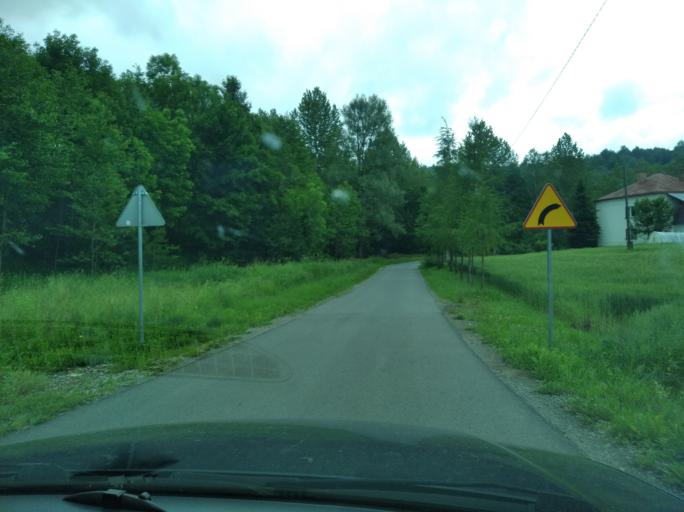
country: PL
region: Subcarpathian Voivodeship
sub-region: Powiat przemyski
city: Nienadowa
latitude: 49.8438
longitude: 22.4138
